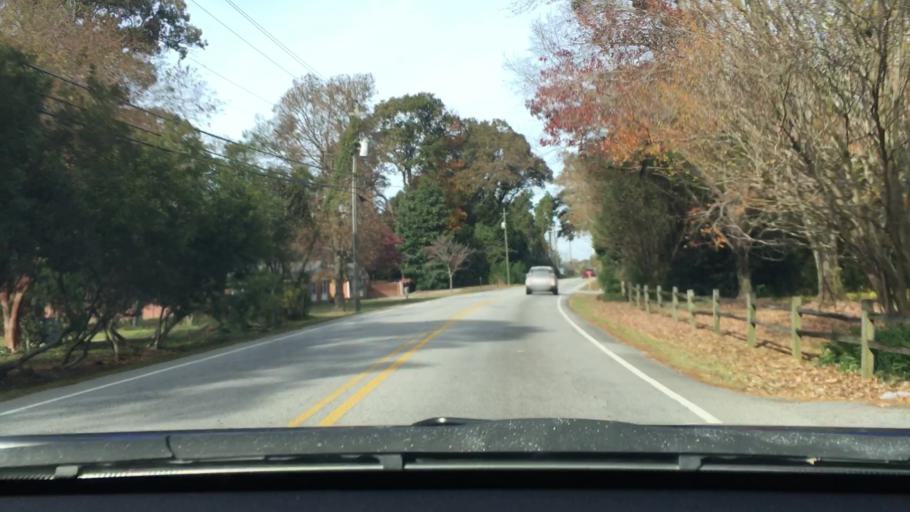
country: US
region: South Carolina
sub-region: Sumter County
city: South Sumter
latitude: 33.8982
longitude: -80.3699
